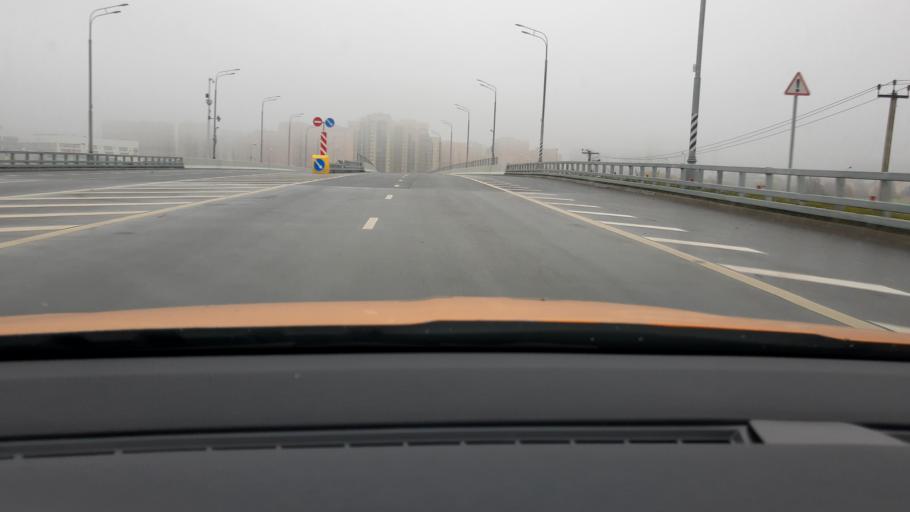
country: RU
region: Moskovskaya
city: Kommunarka
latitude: 55.5607
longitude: 37.4643
